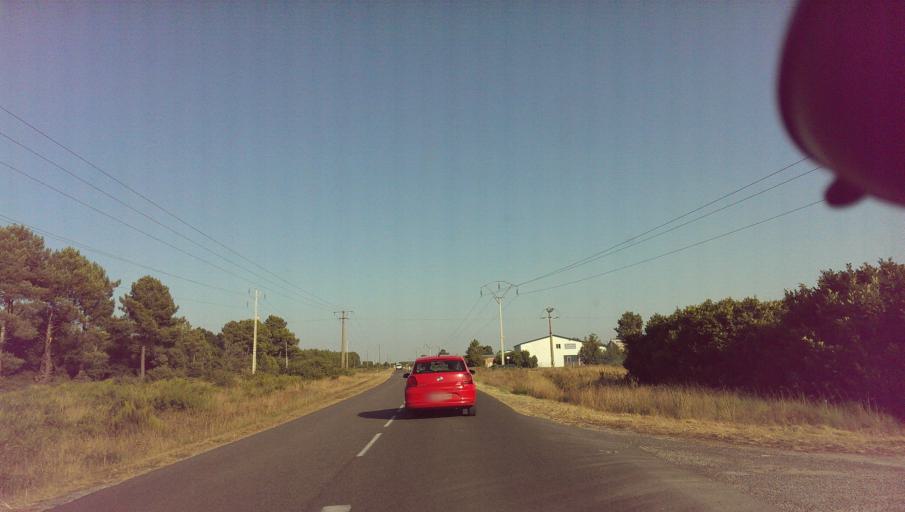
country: FR
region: Aquitaine
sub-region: Departement des Landes
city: Mimizan
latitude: 44.1913
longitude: -1.2167
